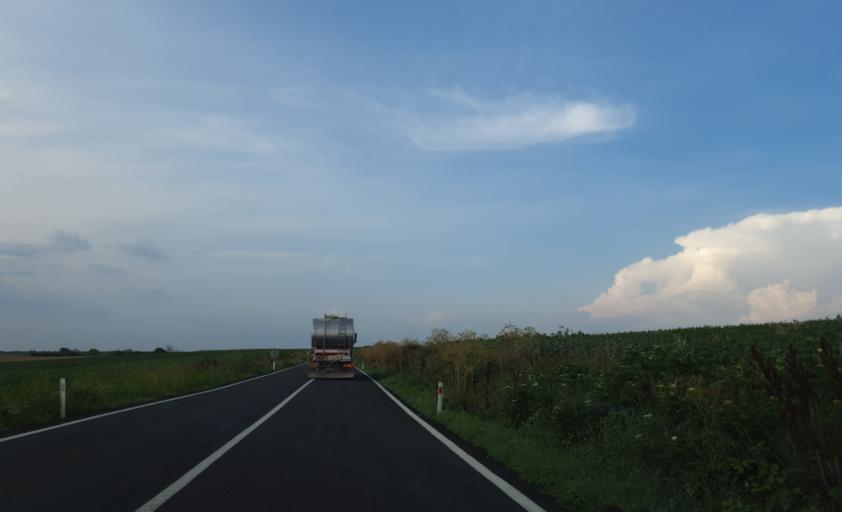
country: TR
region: Tekirdag
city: Hayrabolu
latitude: 41.2618
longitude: 27.1337
